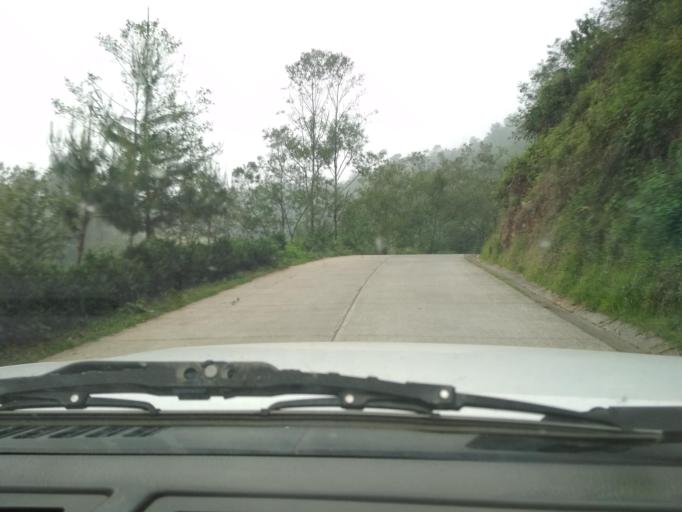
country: MX
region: Veracruz
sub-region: La Perla
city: Chilapa
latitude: 18.9958
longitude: -97.1505
